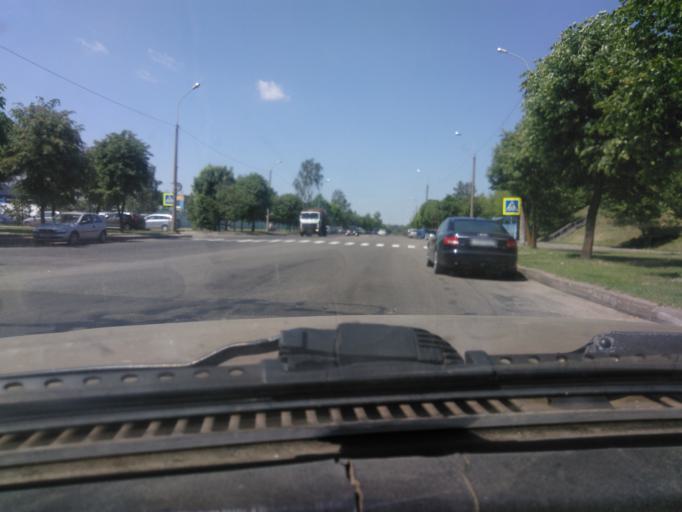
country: BY
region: Mogilev
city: Mahilyow
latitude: 53.9188
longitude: 30.3756
